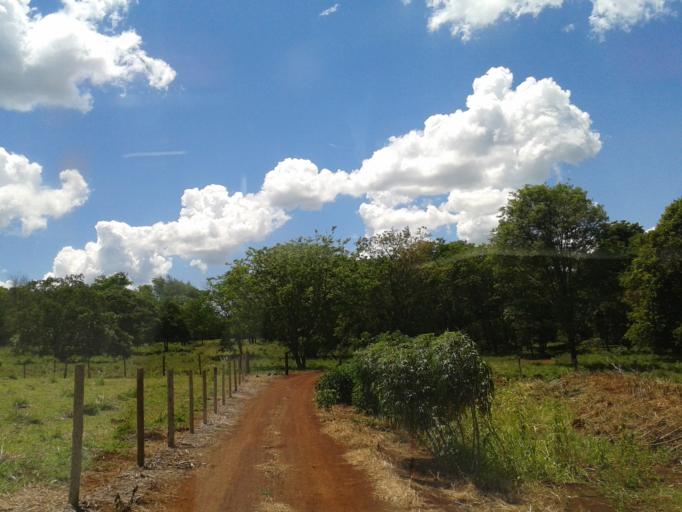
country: BR
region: Minas Gerais
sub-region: Centralina
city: Centralina
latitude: -18.6906
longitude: -49.1781
